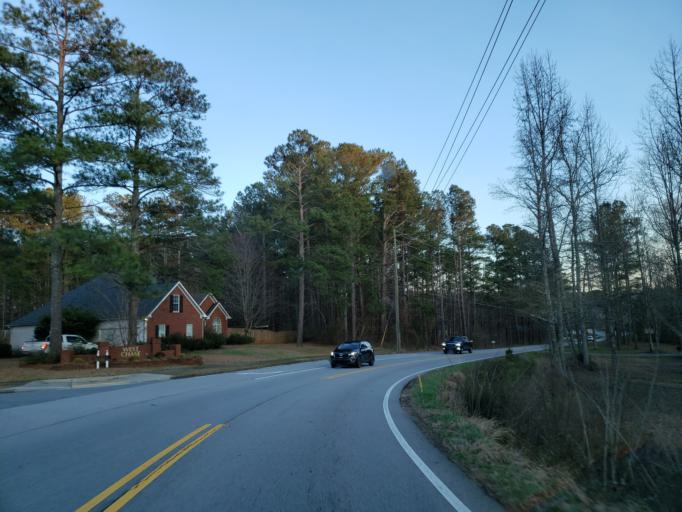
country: US
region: Georgia
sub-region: Cobb County
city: Acworth
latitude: 34.0027
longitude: -84.7385
